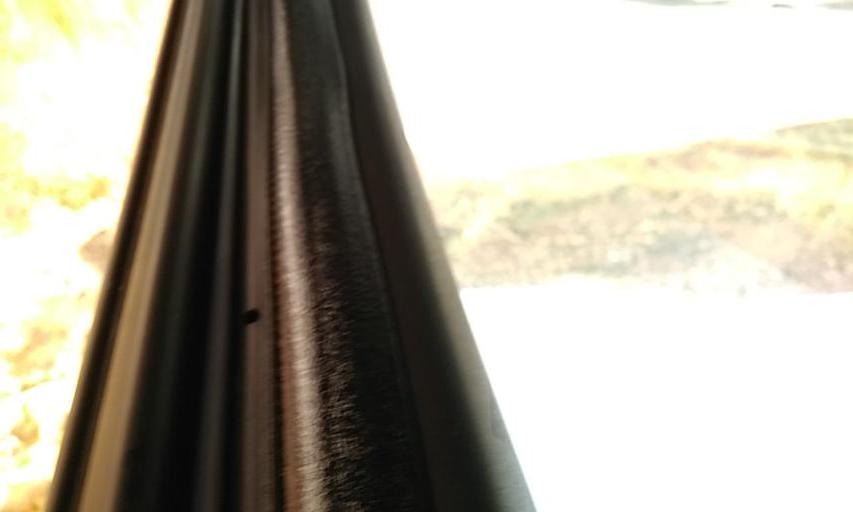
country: GR
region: Crete
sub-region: Nomos Lasithiou
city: Siteia
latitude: 35.1153
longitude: 26.0605
